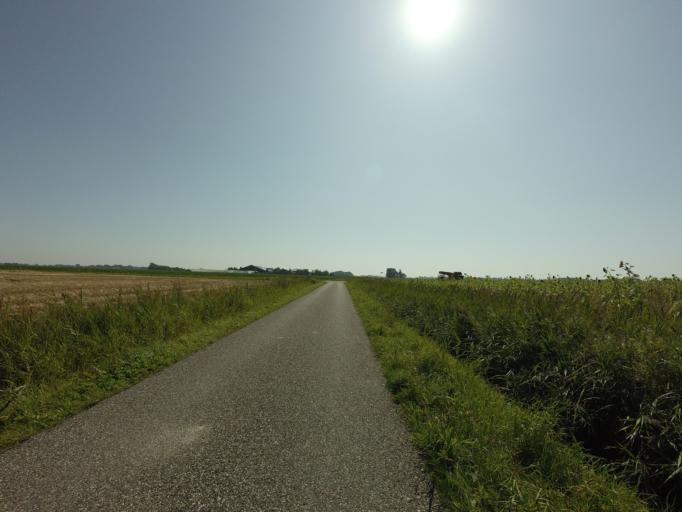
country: NL
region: Friesland
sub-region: Gemeente Dongeradeel
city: Holwerd
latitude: 53.3654
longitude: 5.9290
